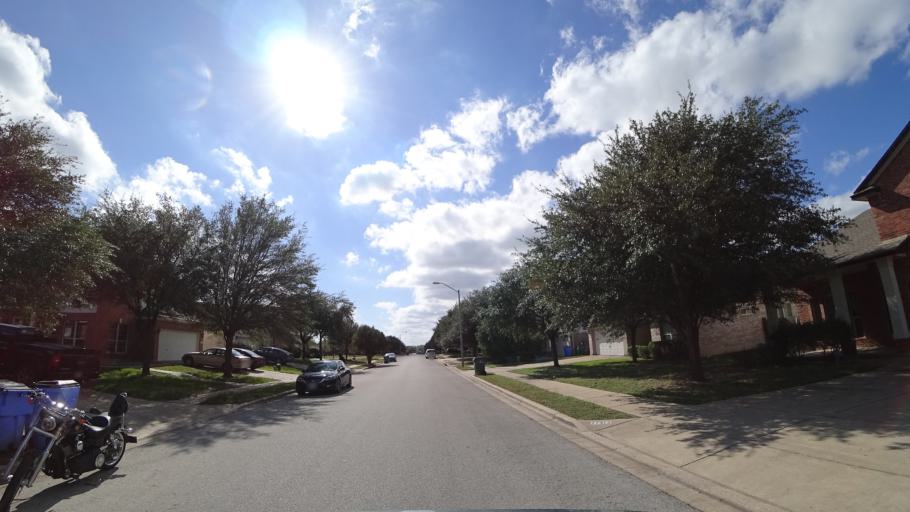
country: US
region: Texas
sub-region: Travis County
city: Windemere
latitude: 30.4757
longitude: -97.6536
